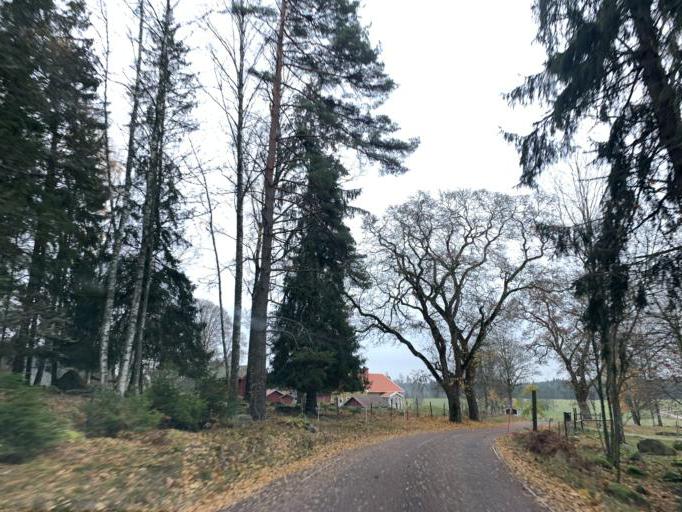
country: SE
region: Vaestmanland
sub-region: Surahammars Kommun
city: Surahammar
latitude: 59.6537
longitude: 16.0737
